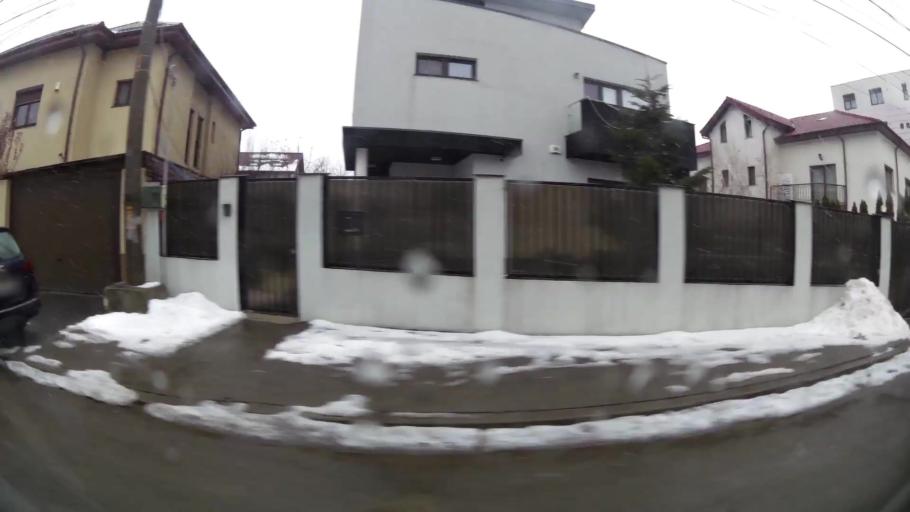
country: RO
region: Ilfov
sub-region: Comuna Otopeni
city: Otopeni
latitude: 44.5013
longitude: 26.0580
